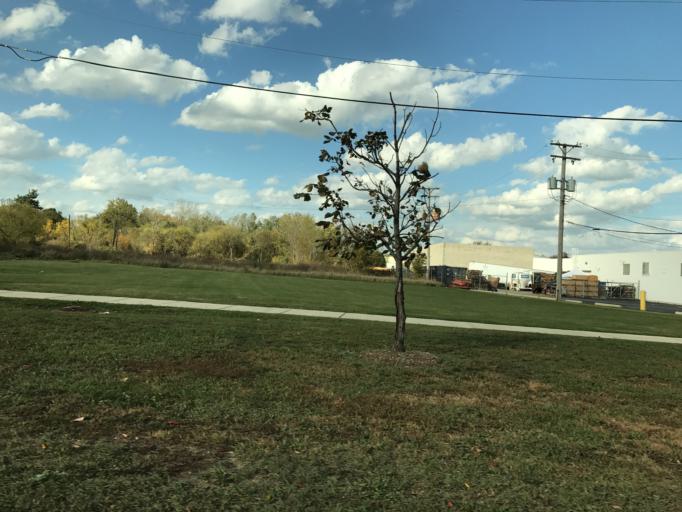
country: US
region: Michigan
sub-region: Oakland County
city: South Lyon
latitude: 42.5095
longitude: -83.6055
